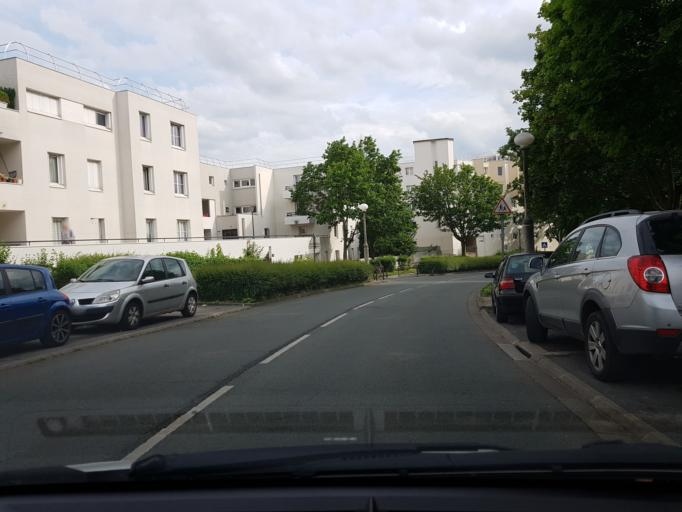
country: FR
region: Ile-de-France
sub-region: Departement de Seine-et-Marne
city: Torcy
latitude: 48.8409
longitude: 2.6509
